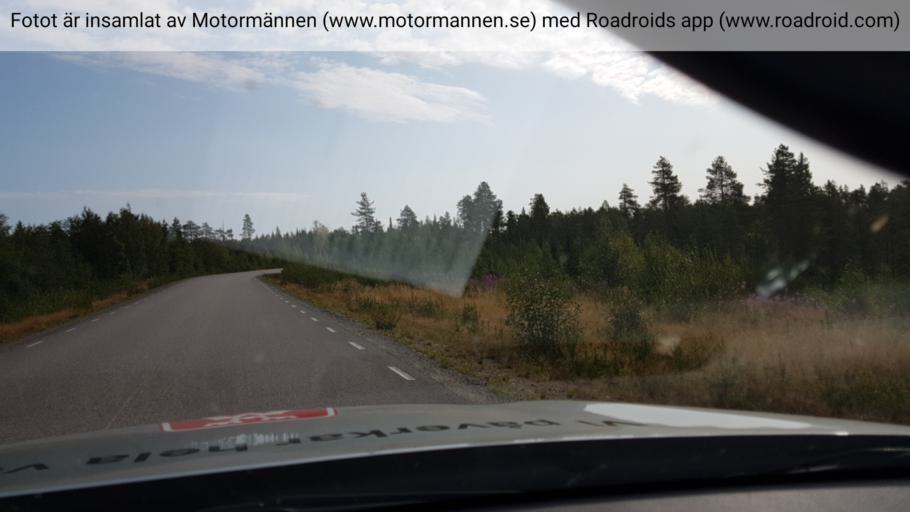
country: SE
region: Vaesterbotten
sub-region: Skelleftea Kommun
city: Storvik
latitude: 65.5190
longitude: 20.5576
